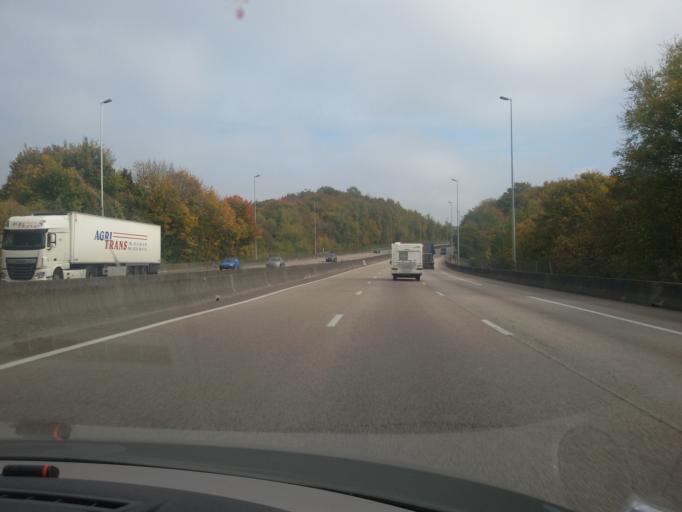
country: FR
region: Haute-Normandie
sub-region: Departement de la Seine-Maritime
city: Sahurs
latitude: 49.3390
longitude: 0.9599
